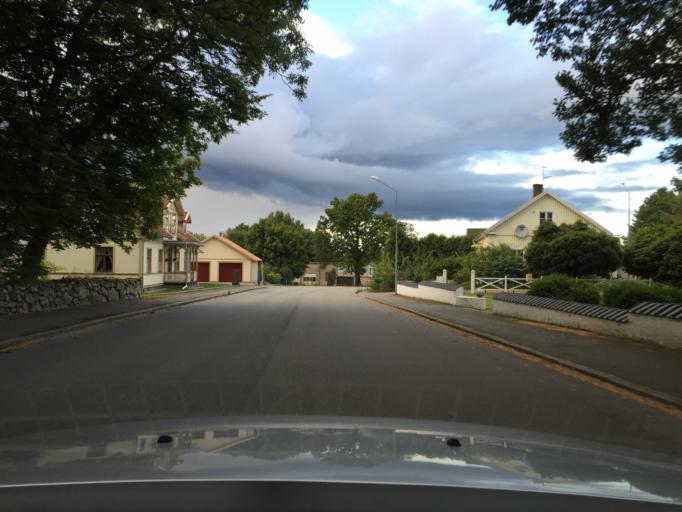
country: SE
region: Skane
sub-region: Hassleholms Kommun
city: Sosdala
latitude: 56.0496
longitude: 13.7188
